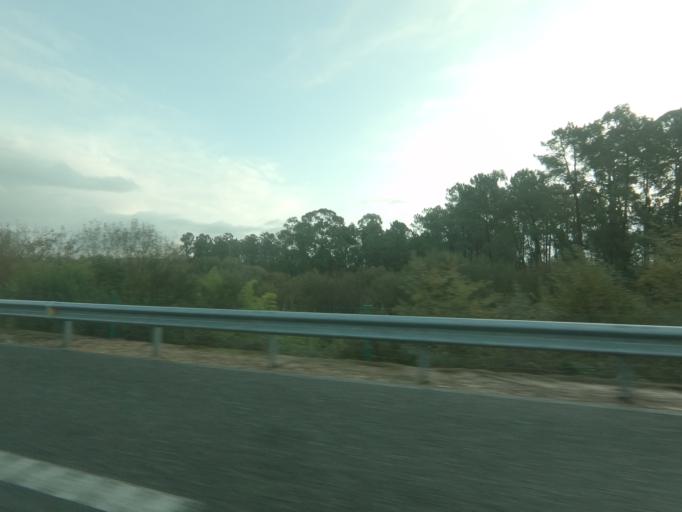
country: ES
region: Galicia
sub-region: Provincia de Pontevedra
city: Tui
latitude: 42.0847
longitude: -8.6394
